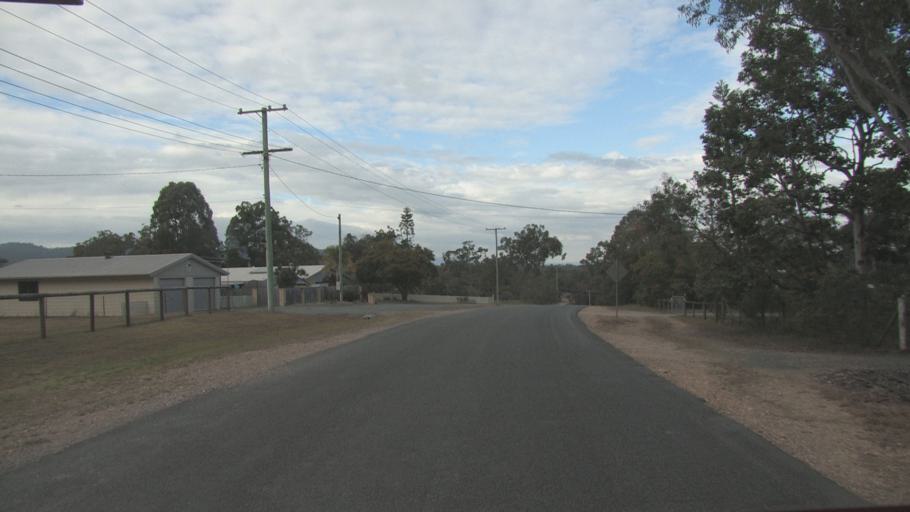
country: AU
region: Queensland
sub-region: Logan
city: Logan Reserve
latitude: -27.7441
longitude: 153.1383
